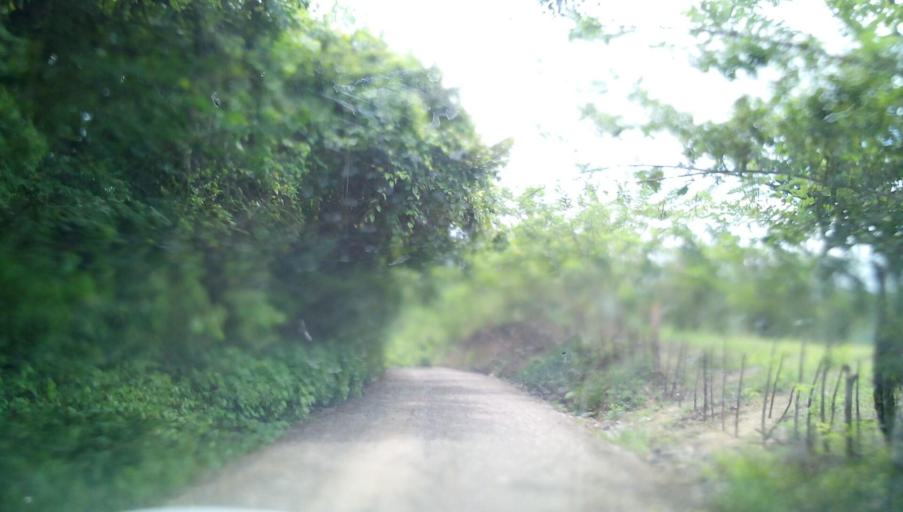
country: MX
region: Veracruz
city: Tepetzintla
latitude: 21.1414
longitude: -97.8526
